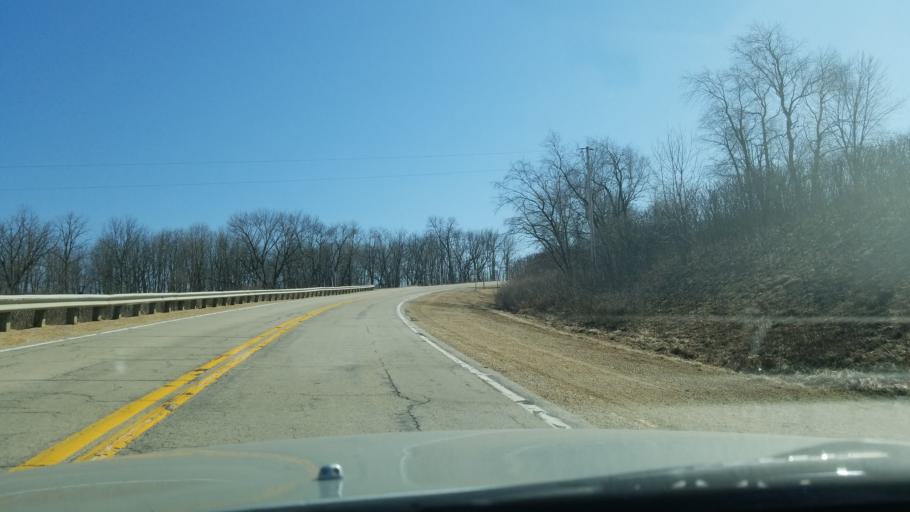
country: US
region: Wisconsin
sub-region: Iowa County
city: Mineral Point
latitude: 42.9023
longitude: -90.2270
